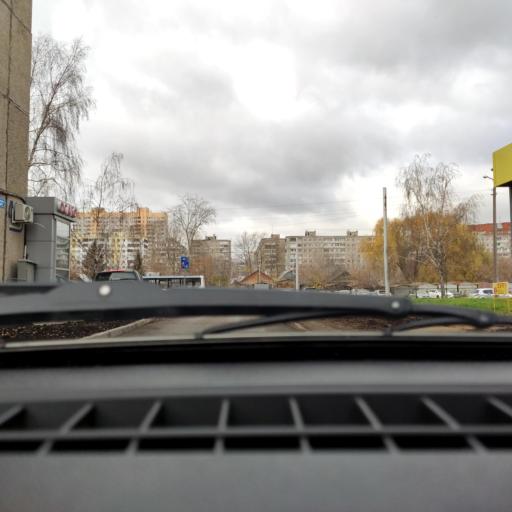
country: RU
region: Bashkortostan
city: Ufa
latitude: 54.7780
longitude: 56.1252
